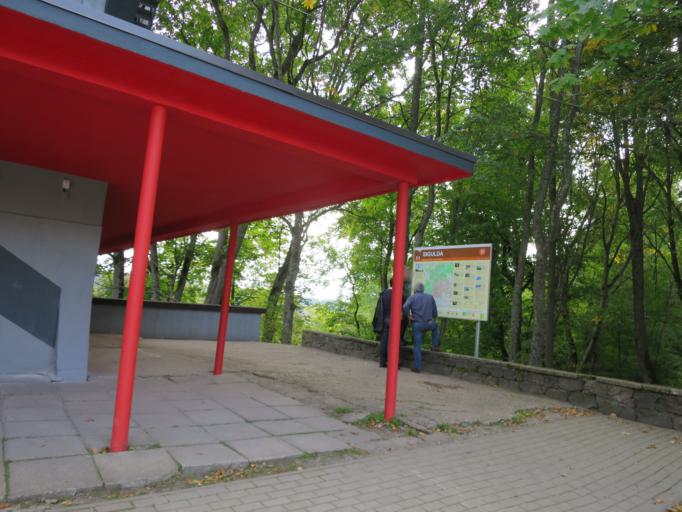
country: LV
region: Sigulda
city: Sigulda
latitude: 57.1695
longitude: 24.8312
